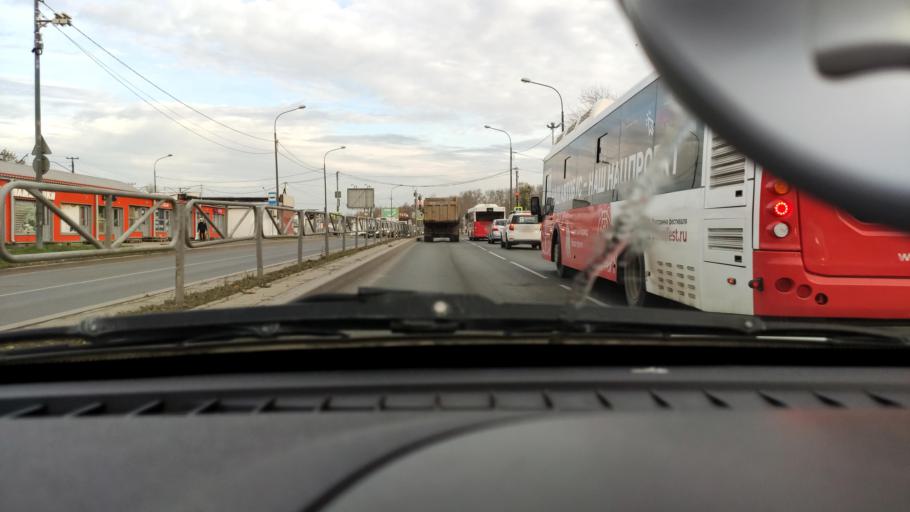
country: RU
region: Perm
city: Perm
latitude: 58.1132
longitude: 56.3661
